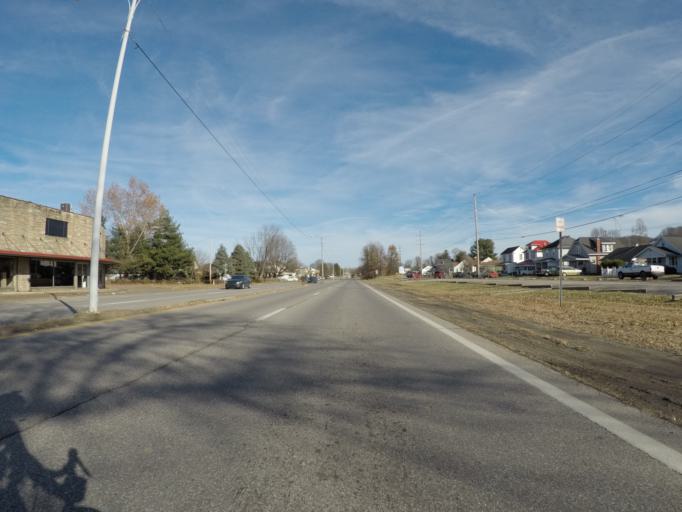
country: US
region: Ohio
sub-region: Lawrence County
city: Burlington
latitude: 38.4013
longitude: -82.5097
